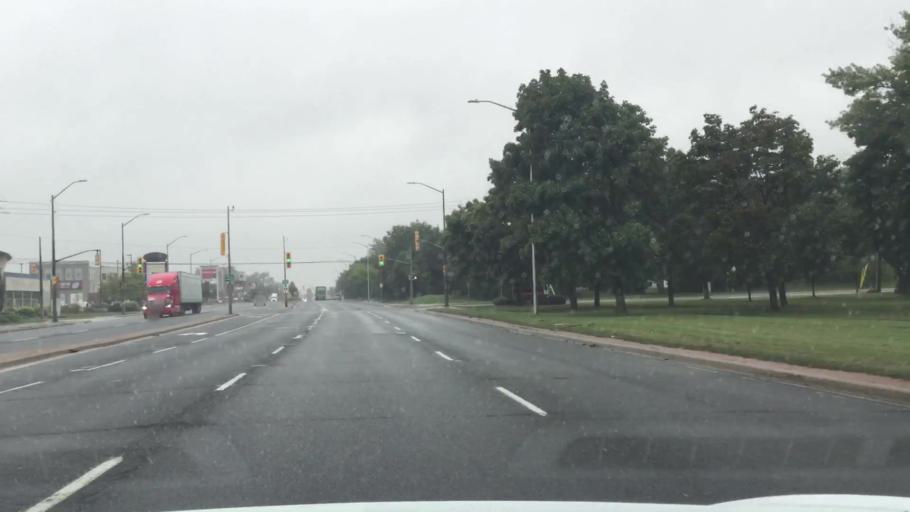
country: CA
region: Ontario
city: Windsor
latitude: 42.2864
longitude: -83.0578
